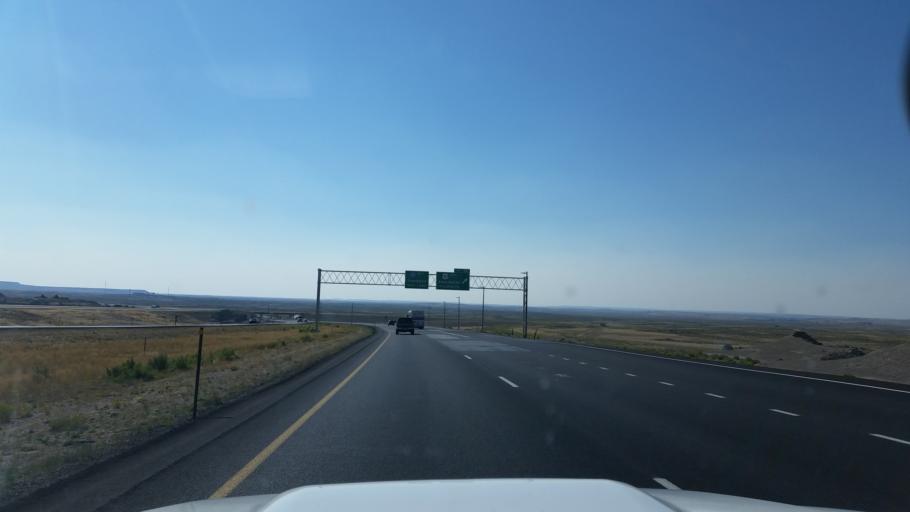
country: US
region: Wyoming
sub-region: Sweetwater County
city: Green River
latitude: 41.5439
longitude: -109.9010
